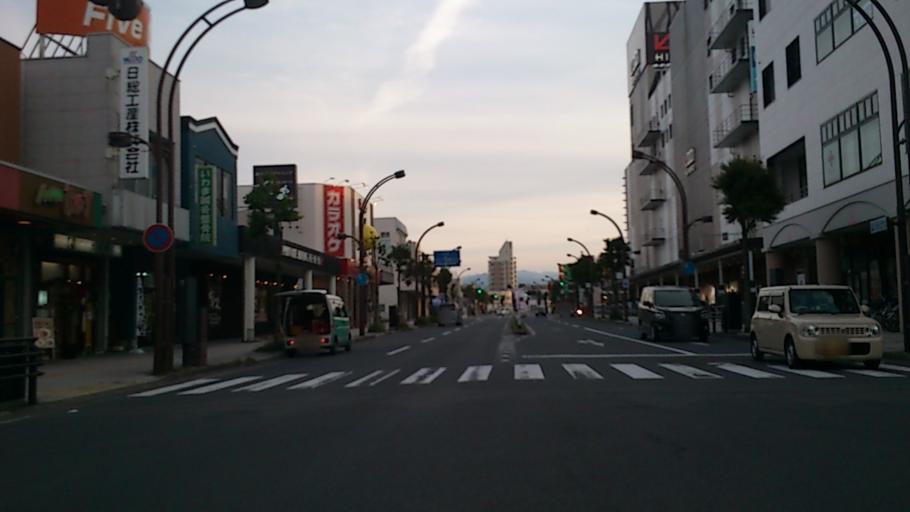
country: JP
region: Aomori
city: Hirosaki
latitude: 40.5977
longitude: 140.4830
